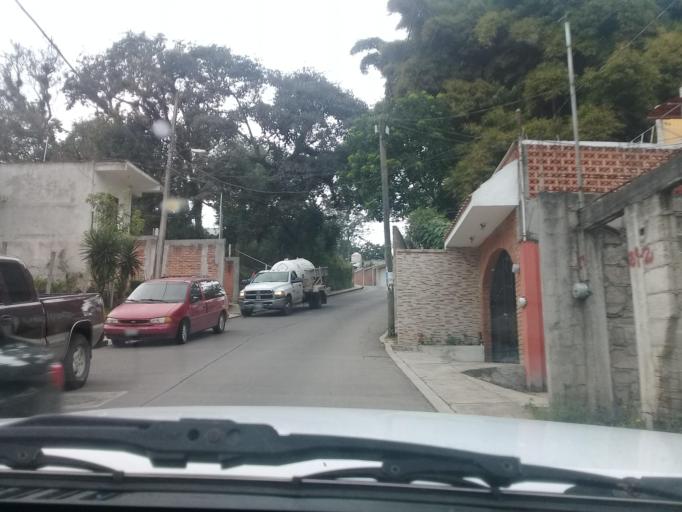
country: MX
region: Veracruz
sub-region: Xalapa
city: Xalapa de Enriquez
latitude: 19.5132
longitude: -96.9118
